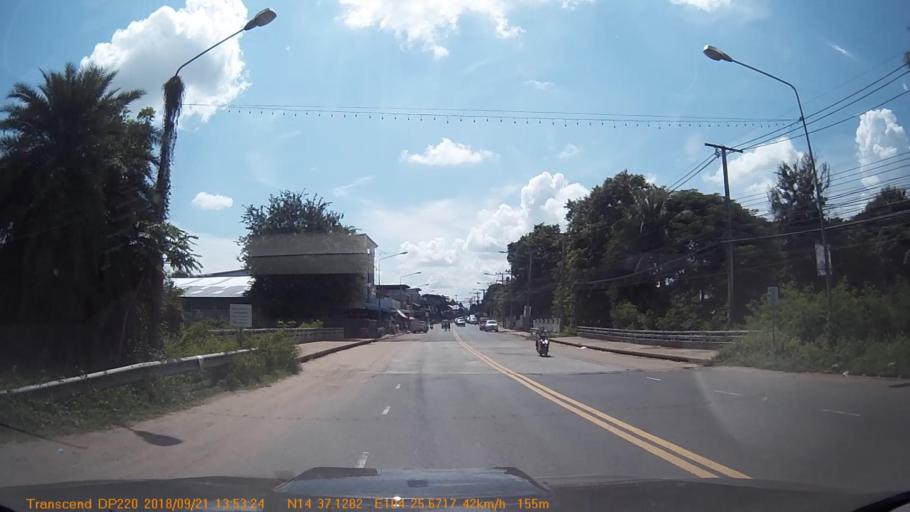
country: TH
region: Sisaket
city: Khun Han
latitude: 14.6187
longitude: 104.4276
